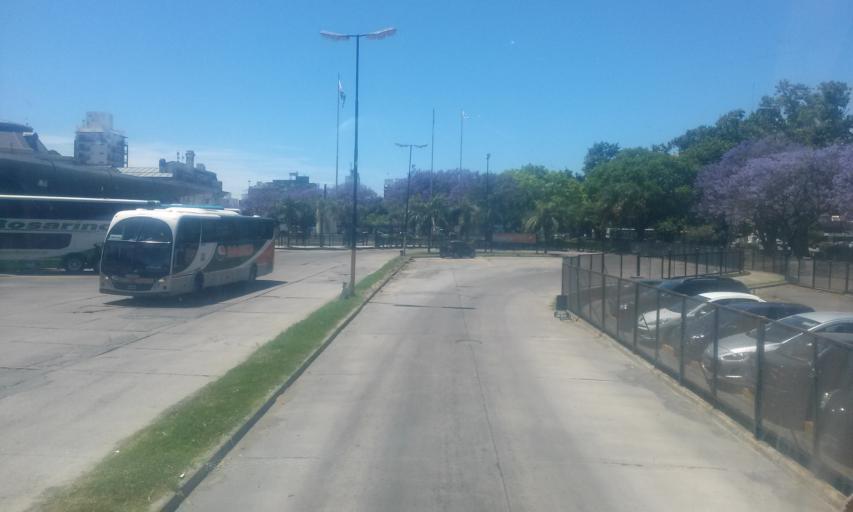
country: AR
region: Santa Fe
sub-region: Departamento de Rosario
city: Rosario
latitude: -32.9398
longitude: -60.6724
